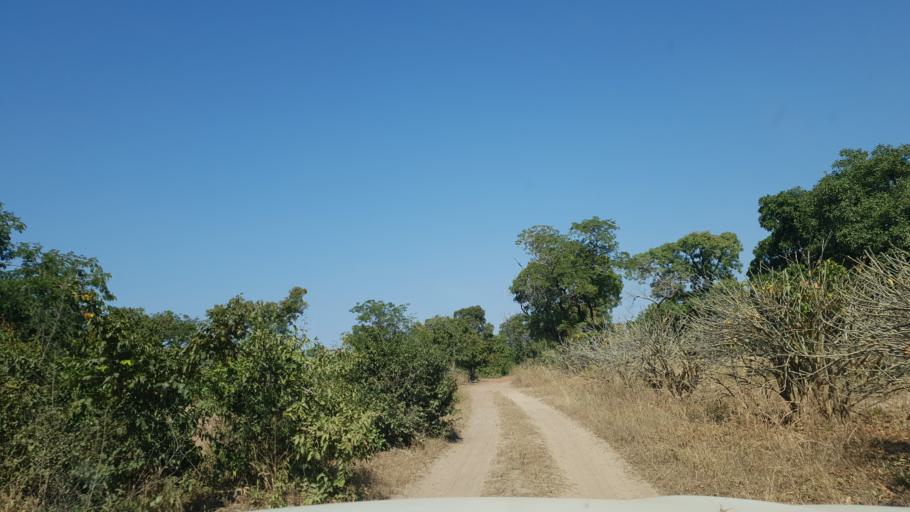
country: ML
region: Sikasso
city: Yorosso
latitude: 12.2709
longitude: -4.6952
